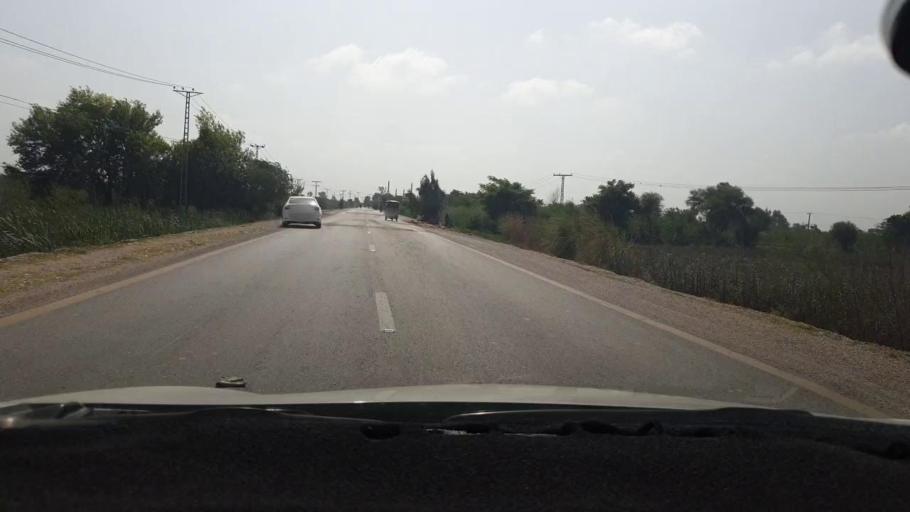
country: PK
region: Sindh
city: Mirpur Khas
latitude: 25.7393
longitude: 69.0946
